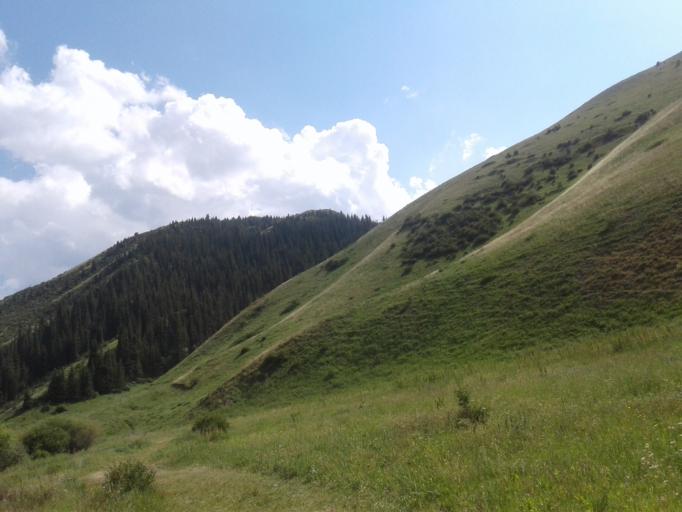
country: KG
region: Naryn
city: Naryn
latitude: 41.4586
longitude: 76.4529
